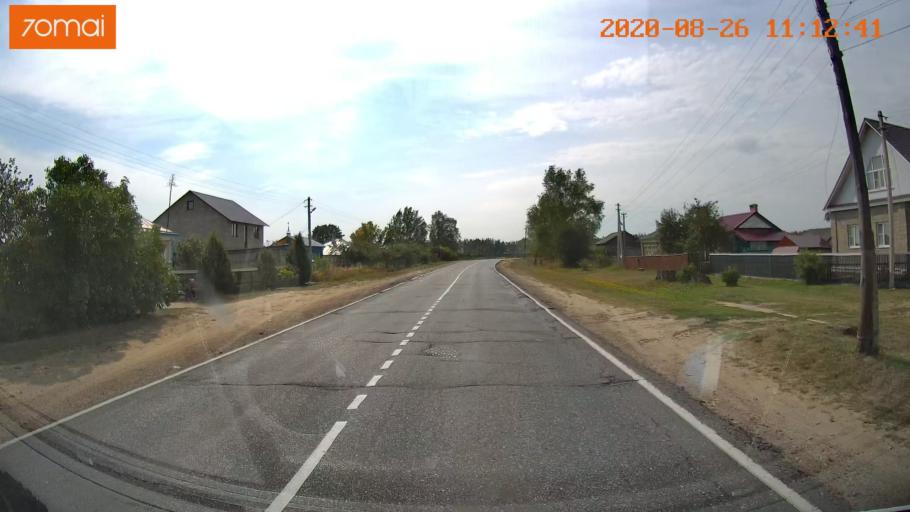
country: RU
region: Rjazan
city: Izhevskoye
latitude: 54.4676
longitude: 41.1246
